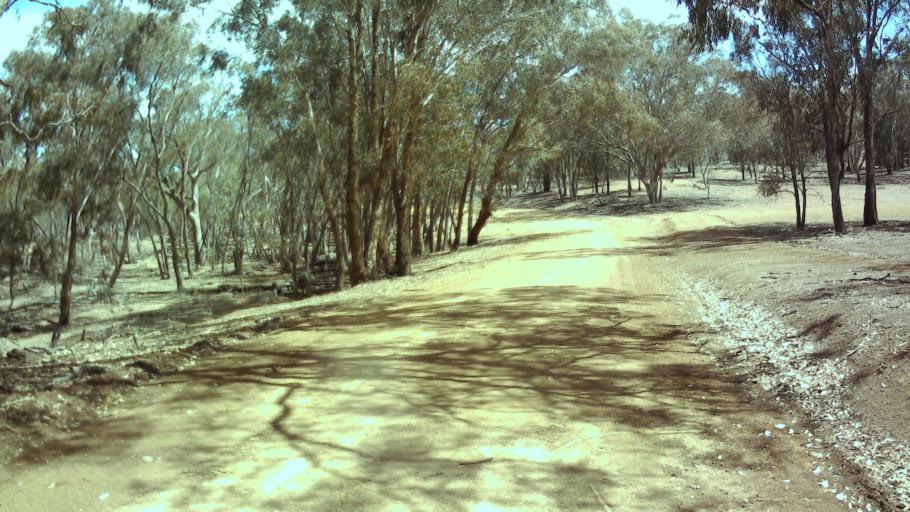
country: AU
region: New South Wales
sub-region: Weddin
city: Grenfell
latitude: -33.7989
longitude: 148.1602
